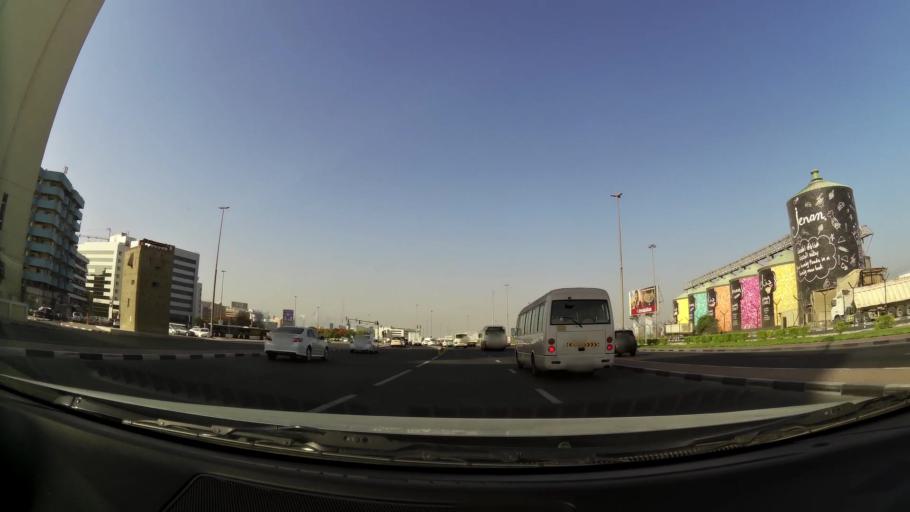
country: AE
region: Ash Shariqah
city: Sharjah
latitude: 25.2620
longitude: 55.2843
